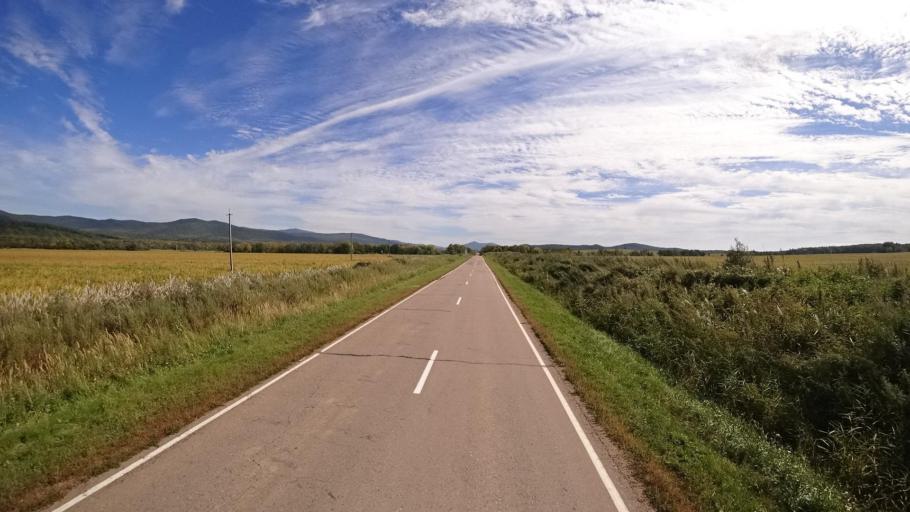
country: RU
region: Primorskiy
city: Yakovlevka
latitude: 44.4243
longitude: 133.5762
